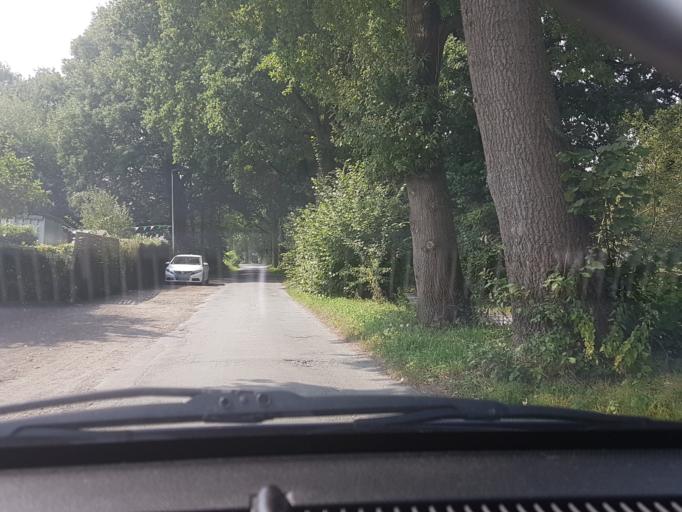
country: DE
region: North Rhine-Westphalia
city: Emsdetten
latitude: 52.1602
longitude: 7.5075
